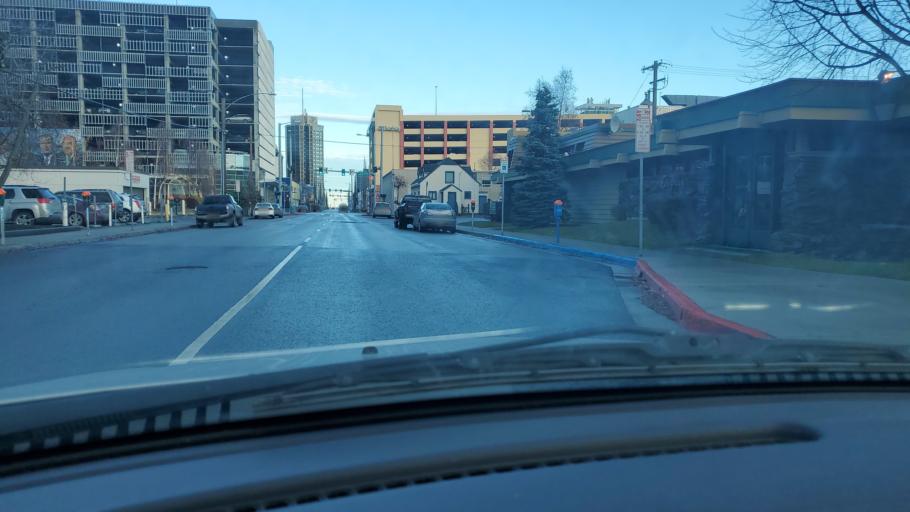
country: US
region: Alaska
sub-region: Anchorage Municipality
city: Anchorage
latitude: 61.2147
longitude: -149.8915
